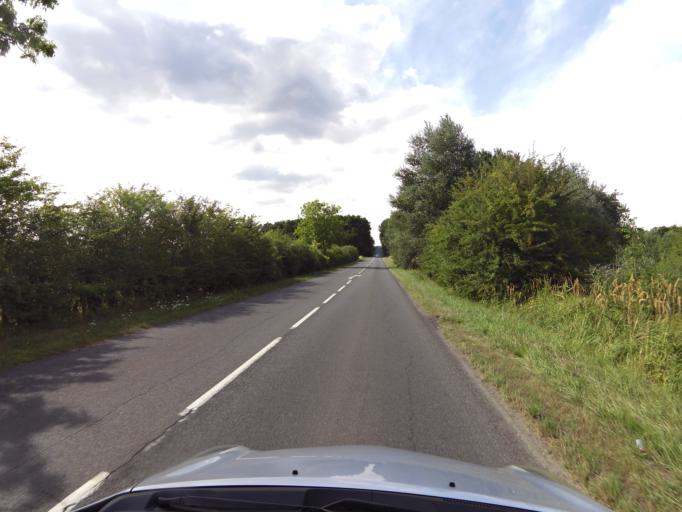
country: FR
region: Picardie
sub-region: Departement de l'Aisne
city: Bruyeres-et-Montberault
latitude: 49.5365
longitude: 3.6464
